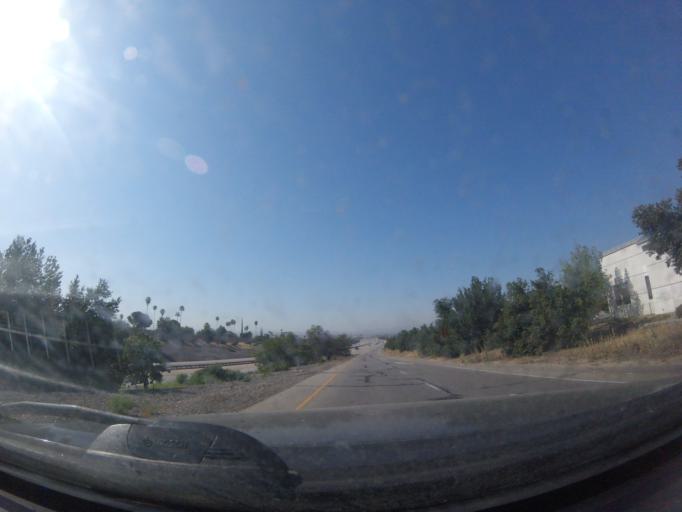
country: US
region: California
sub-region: San Bernardino County
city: Highland
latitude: 34.1207
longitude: -117.2015
